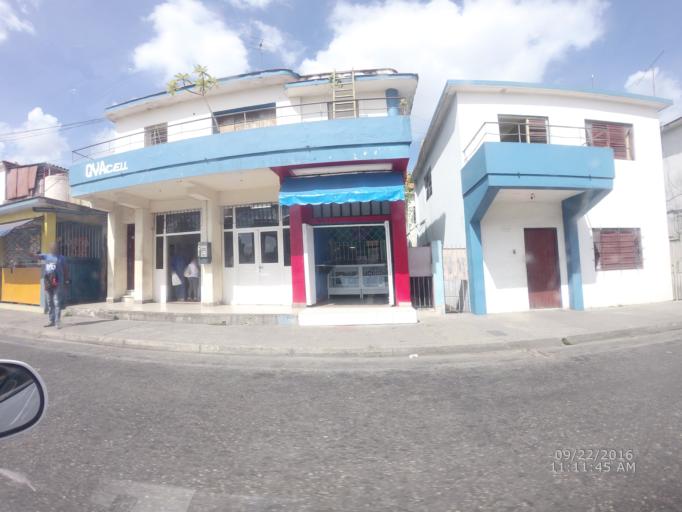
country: CU
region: La Habana
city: Cerro
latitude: 23.0947
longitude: -82.4218
